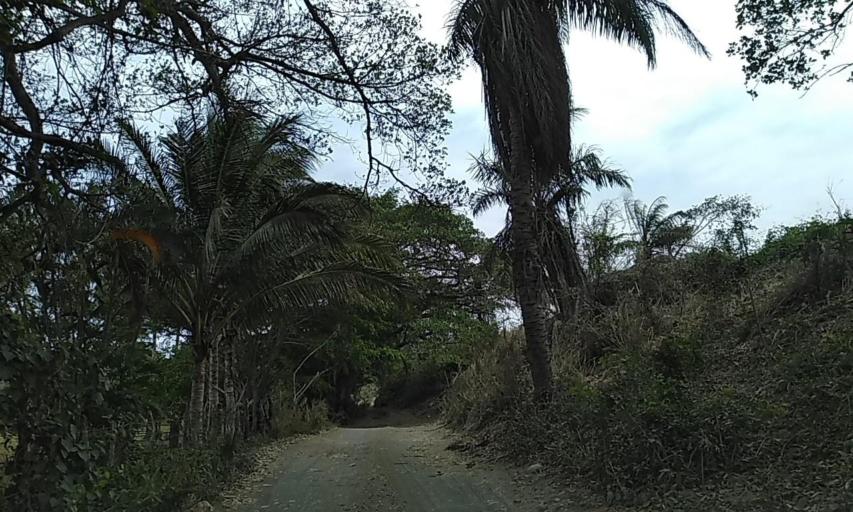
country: MX
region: Veracruz
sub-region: La Antigua
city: Nicolas Blanco (San Pancho)
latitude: 19.3108
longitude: -96.3055
